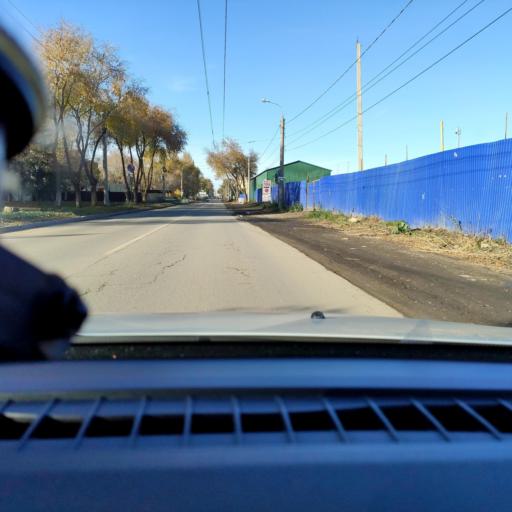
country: RU
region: Samara
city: Samara
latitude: 53.1955
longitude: 50.2720
